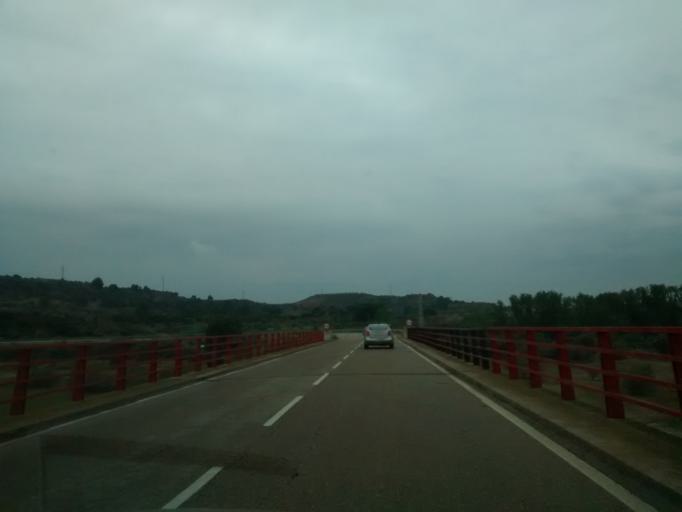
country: ES
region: Aragon
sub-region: Provincia de Zaragoza
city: Caspe
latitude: 41.2605
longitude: -0.0627
